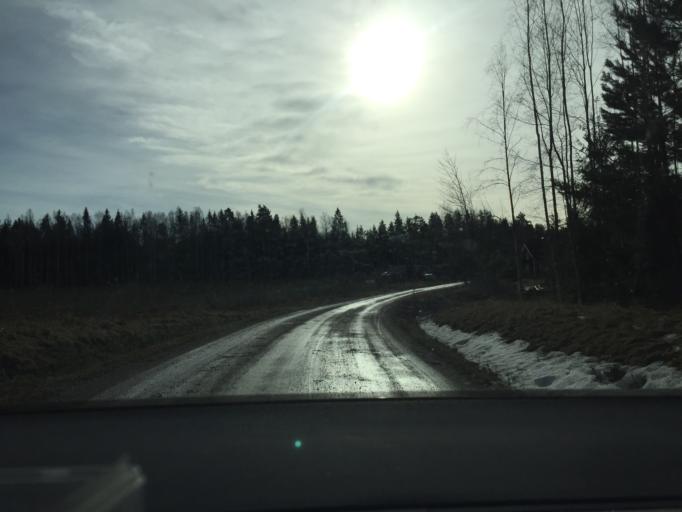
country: SE
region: OErebro
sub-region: Orebro Kommun
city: Odensbacken
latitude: 59.1208
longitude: 15.4727
